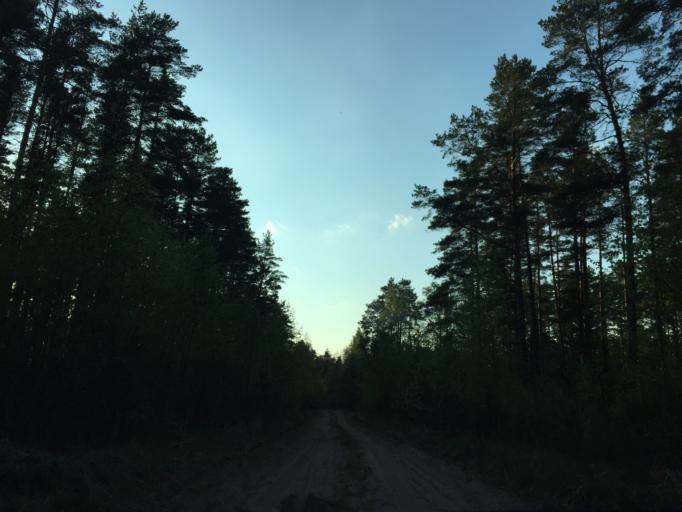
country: LV
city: Tireli
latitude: 56.8714
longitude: 23.6837
